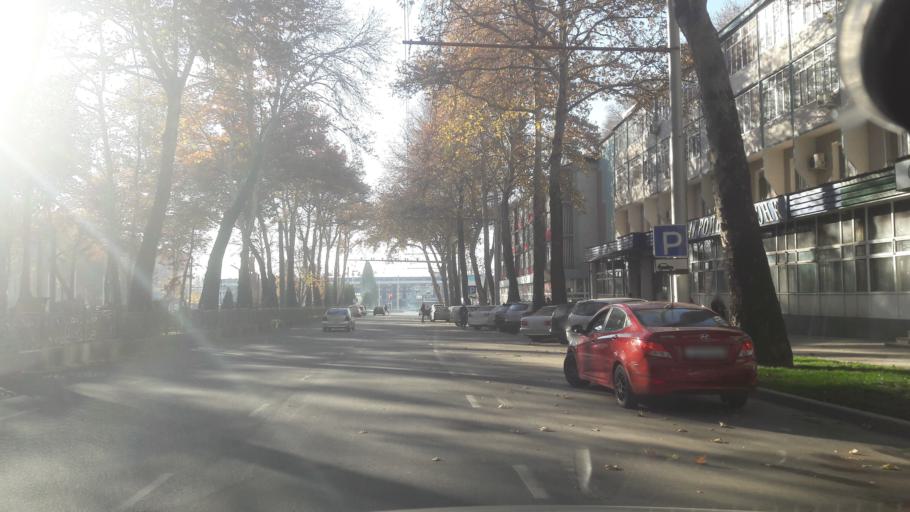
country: TJ
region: Dushanbe
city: Dushanbe
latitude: 38.5597
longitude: 68.7991
